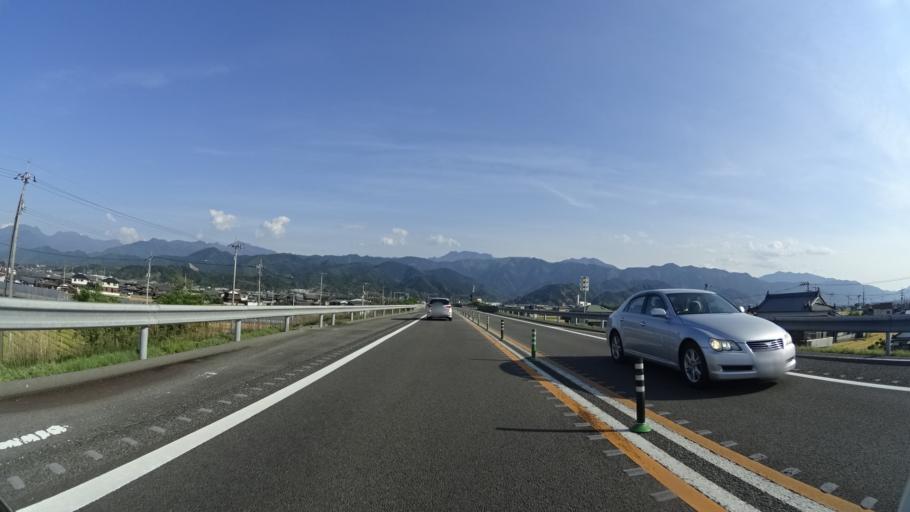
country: JP
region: Ehime
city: Saijo
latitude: 33.9024
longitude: 133.0757
